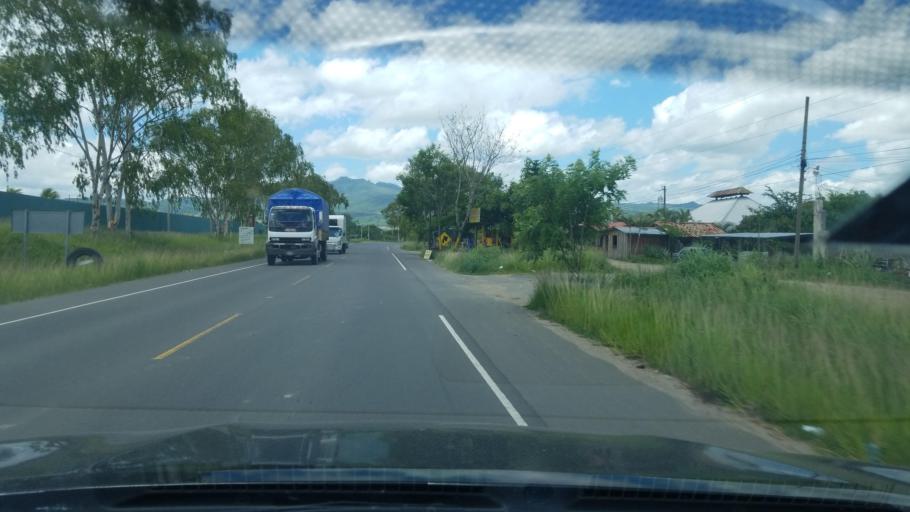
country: HN
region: Francisco Morazan
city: Cofradia
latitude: 14.2880
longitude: -87.2429
